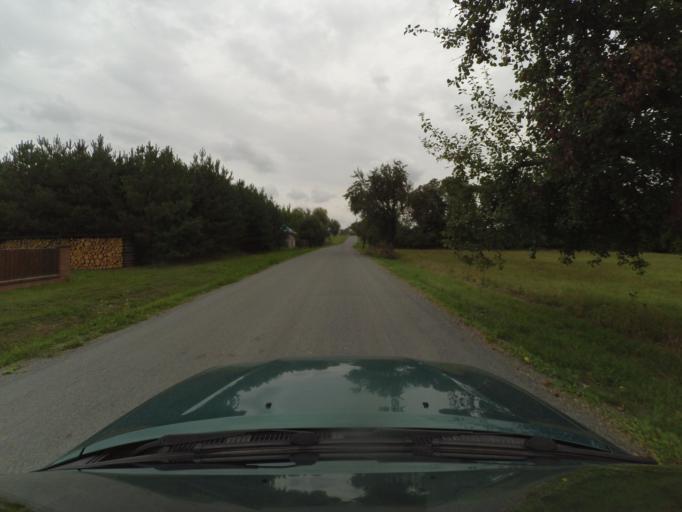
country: CZ
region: Plzensky
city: Kozlany
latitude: 49.9639
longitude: 13.5338
